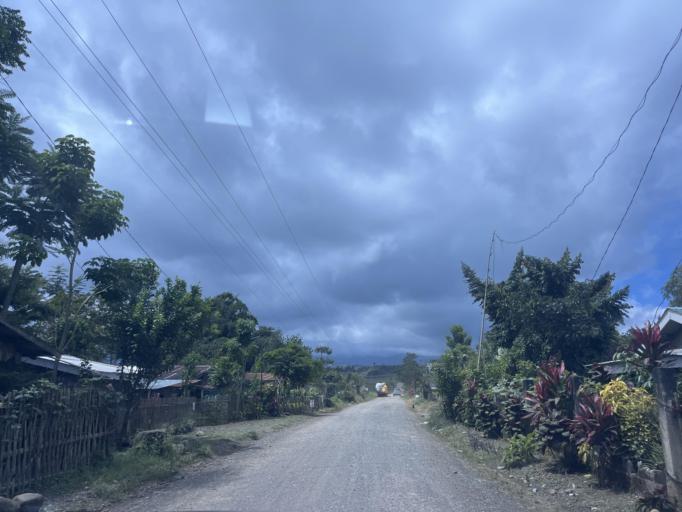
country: PH
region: Northern Mindanao
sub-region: Province of Bukidnon
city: Impalutao
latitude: 8.2213
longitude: 124.9952
